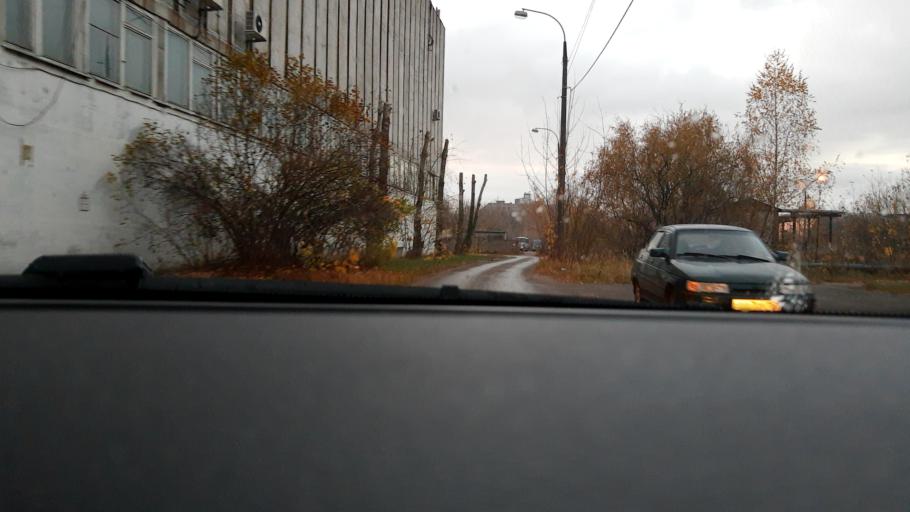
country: RU
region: Nizjnij Novgorod
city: Gorbatovka
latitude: 56.3588
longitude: 43.8346
